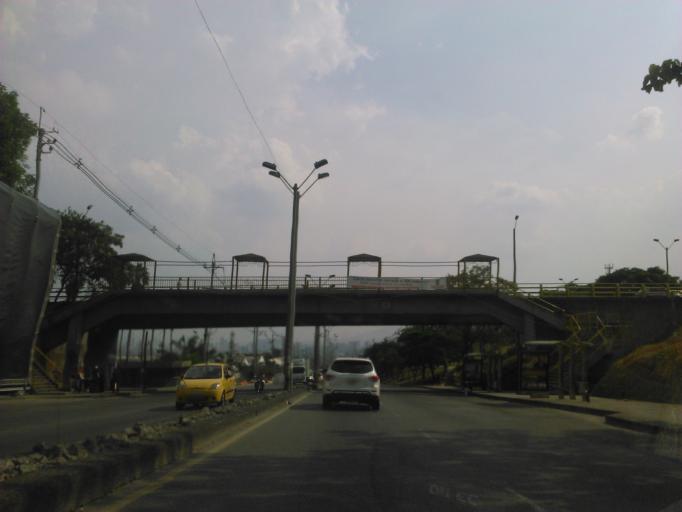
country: CO
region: Antioquia
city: Medellin
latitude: 6.2927
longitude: -75.5682
